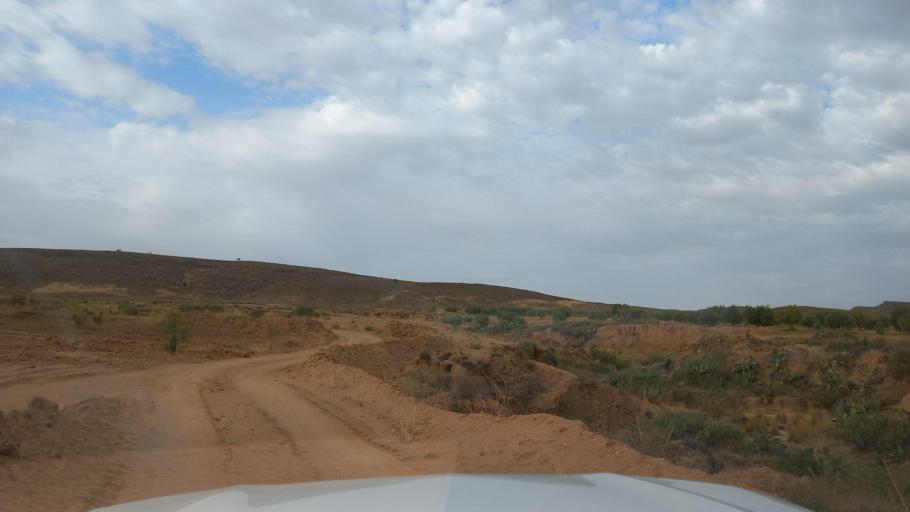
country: TN
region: Al Qasrayn
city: Kasserine
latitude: 35.1864
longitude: 9.0474
